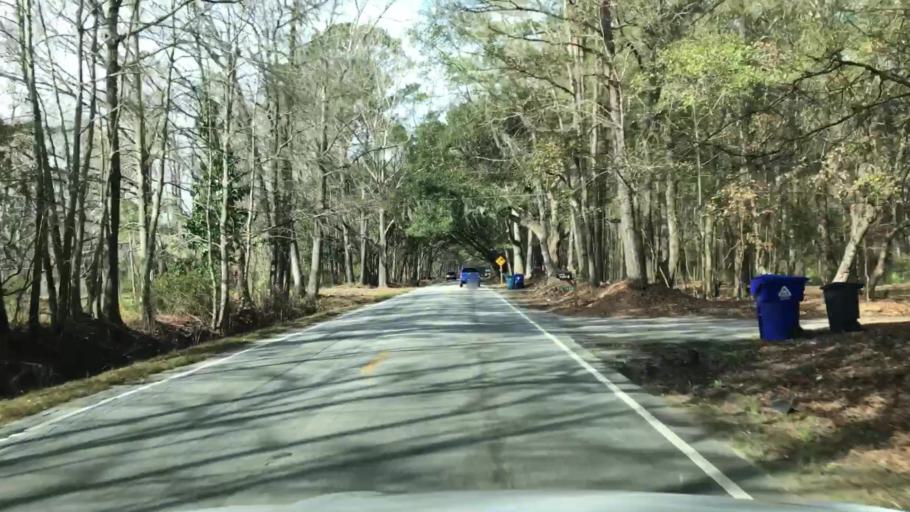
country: US
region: South Carolina
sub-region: Charleston County
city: Shell Point
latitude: 32.7561
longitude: -80.0509
